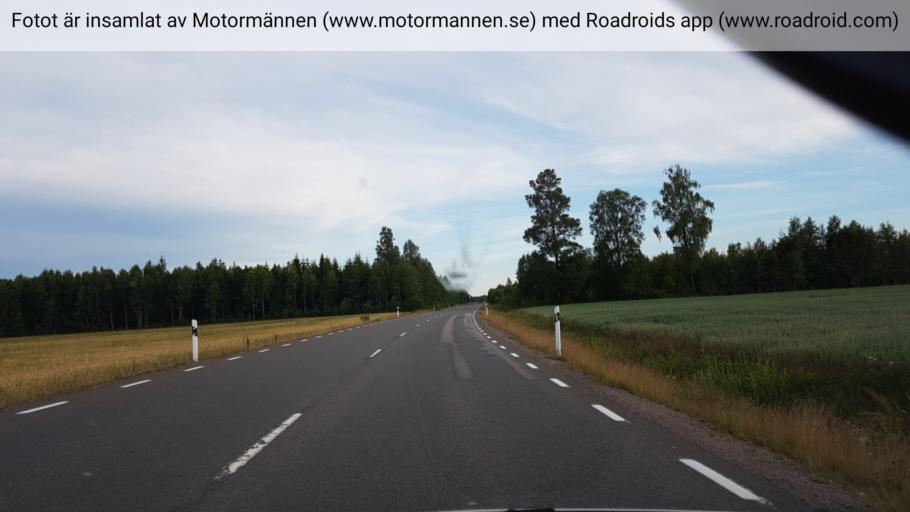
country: SE
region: Vaestra Goetaland
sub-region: Tibro Kommun
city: Tibro
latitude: 58.4990
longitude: 14.1664
